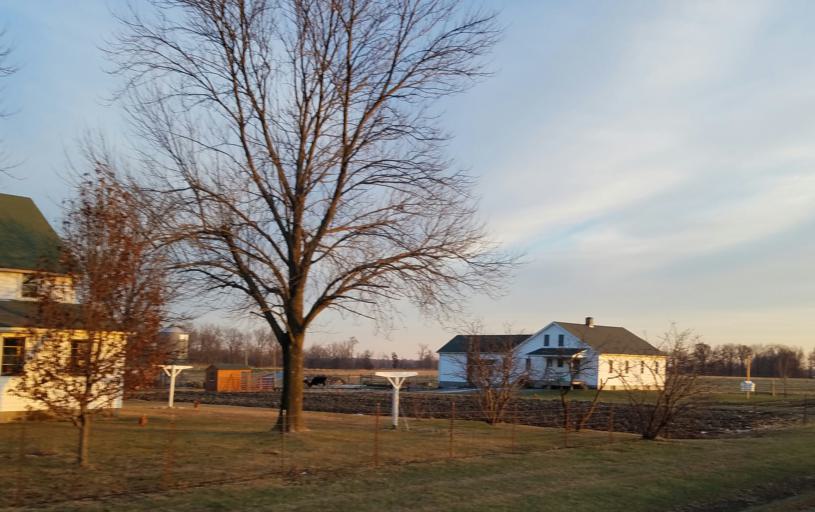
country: US
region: Missouri
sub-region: Boone County
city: Centralia
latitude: 39.3038
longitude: -92.2851
